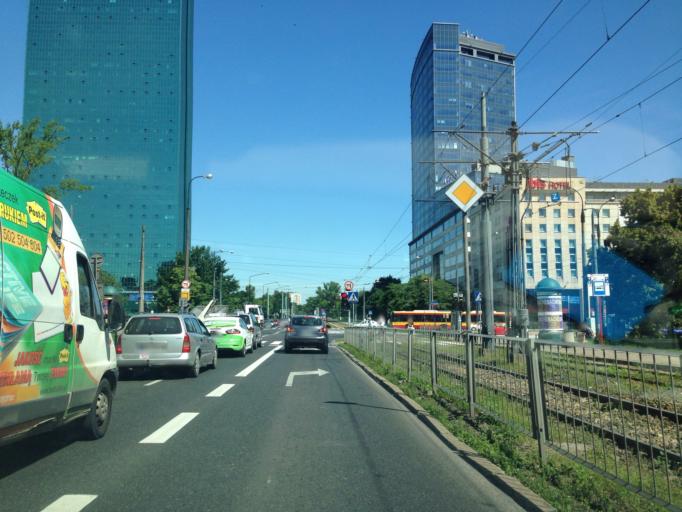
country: PL
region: Masovian Voivodeship
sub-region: Warszawa
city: Wola
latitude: 52.2529
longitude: 20.9979
